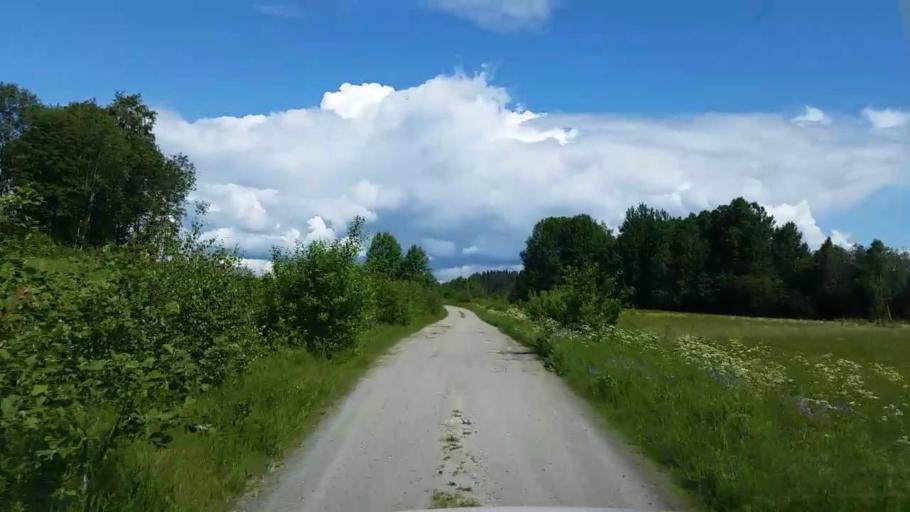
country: SE
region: Vaestmanland
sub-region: Fagersta Kommun
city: Fagersta
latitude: 59.9667
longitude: 15.7361
